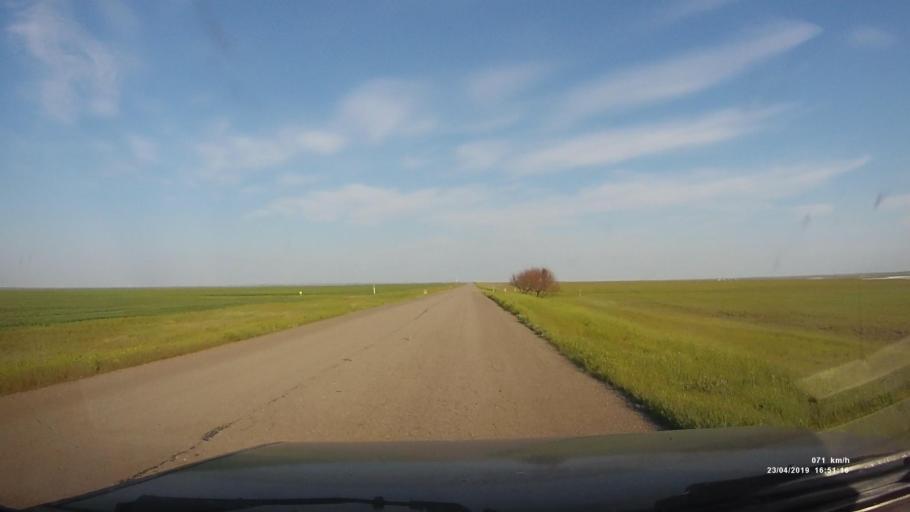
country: RU
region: Kalmykiya
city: Priyutnoye
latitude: 46.3237
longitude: 43.3035
